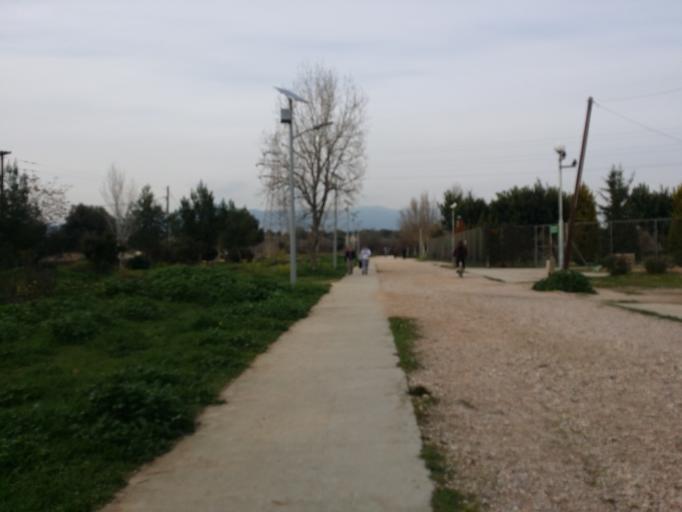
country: GR
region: Attica
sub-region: Nomarchia Athinas
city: Agioi Anargyroi
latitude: 38.0376
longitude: 23.7182
